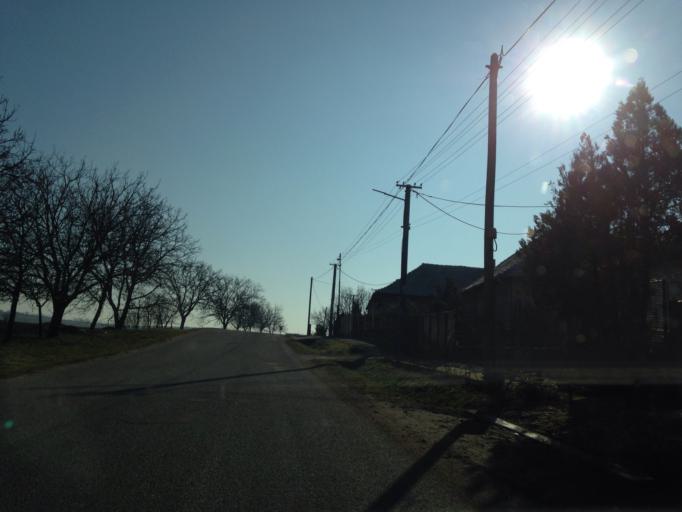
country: SK
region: Nitriansky
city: Svodin
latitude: 47.9189
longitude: 18.4040
